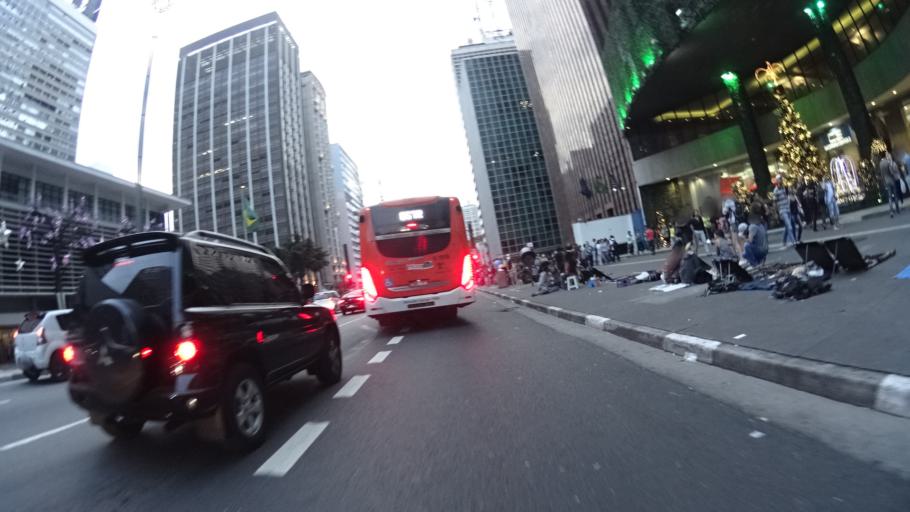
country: BR
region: Sao Paulo
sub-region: Sao Paulo
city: Sao Paulo
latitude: -23.5587
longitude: -46.6596
